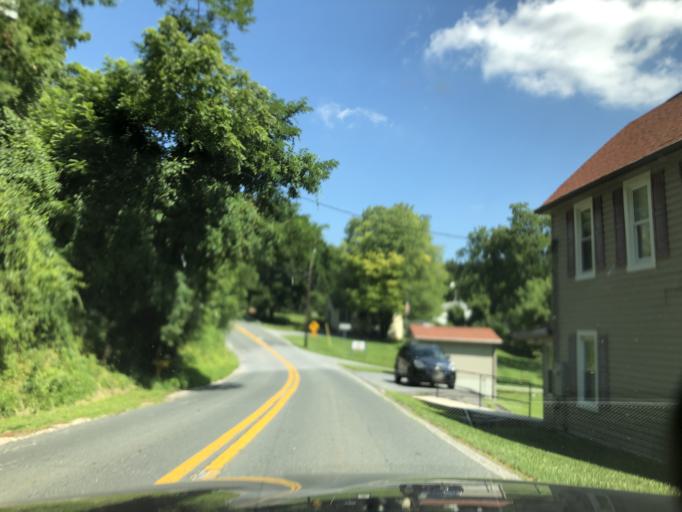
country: US
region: Maryland
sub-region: Carroll County
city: Westminster
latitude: 39.5919
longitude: -76.9686
